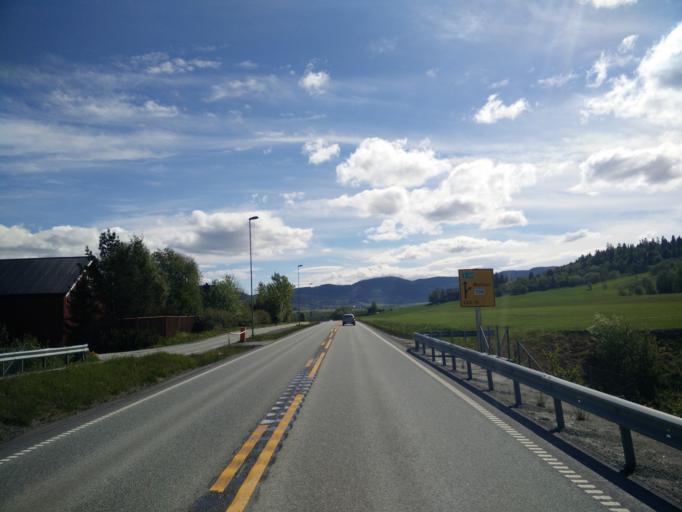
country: NO
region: Sor-Trondelag
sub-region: Melhus
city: Melhus
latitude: 63.3227
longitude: 10.2542
